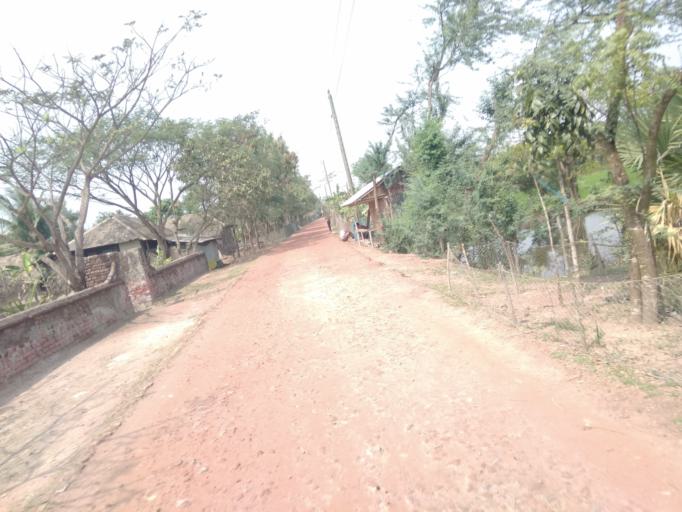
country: IN
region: West Bengal
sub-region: North 24 Parganas
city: Taki
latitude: 22.3010
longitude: 89.2682
